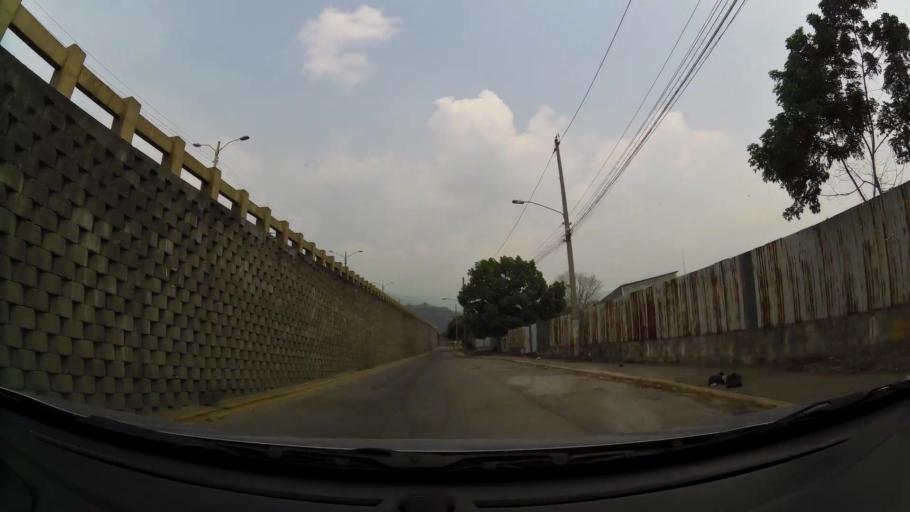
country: HN
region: Cortes
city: San Pedro Sula
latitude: 15.4771
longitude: -88.0322
